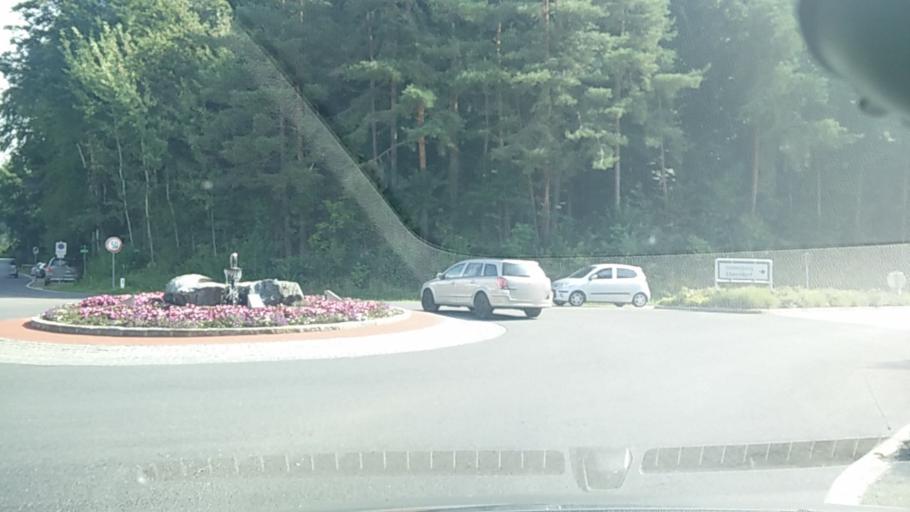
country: AT
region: Carinthia
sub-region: Politischer Bezirk Volkermarkt
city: Eberndorf
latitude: 46.6090
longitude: 14.5754
